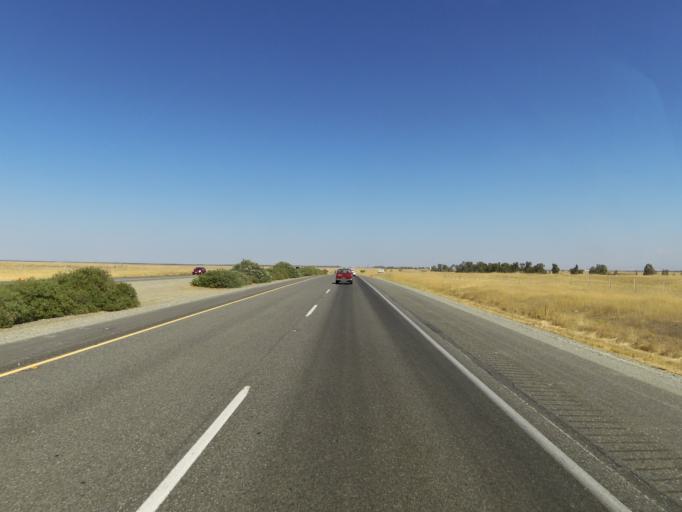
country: US
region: California
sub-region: Glenn County
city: Orland
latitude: 39.8060
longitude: -122.1998
